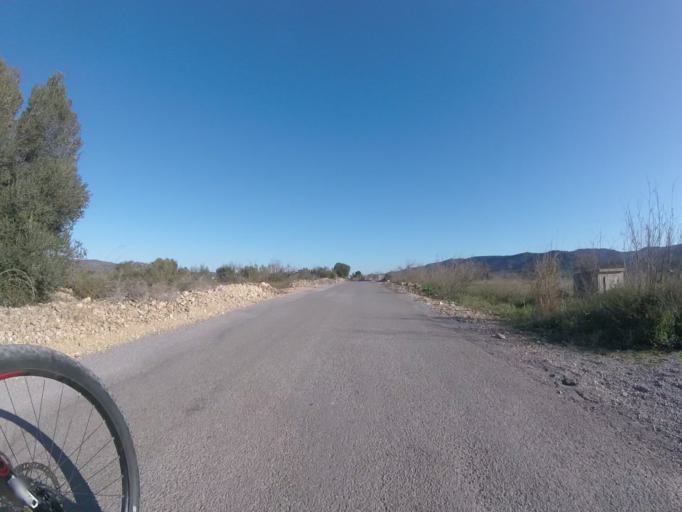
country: ES
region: Valencia
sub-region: Provincia de Castello
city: Alcala de Xivert
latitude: 40.2930
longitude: 0.2176
